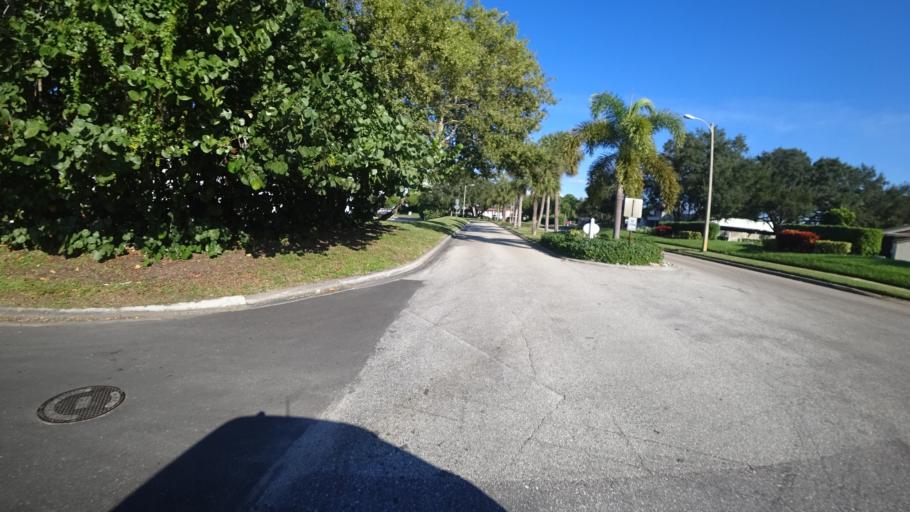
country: US
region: Florida
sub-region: Manatee County
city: West Bradenton
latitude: 27.4752
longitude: -82.6220
